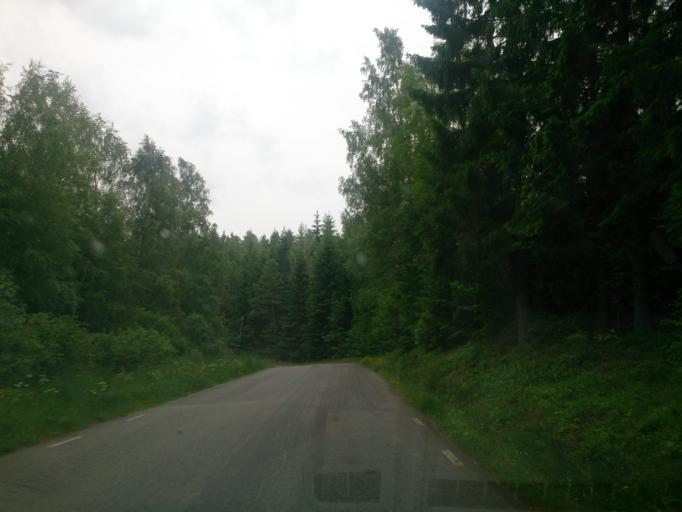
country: SE
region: OEstergoetland
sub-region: Soderkopings Kommun
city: Soederkoeping
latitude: 58.3191
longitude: 16.2881
